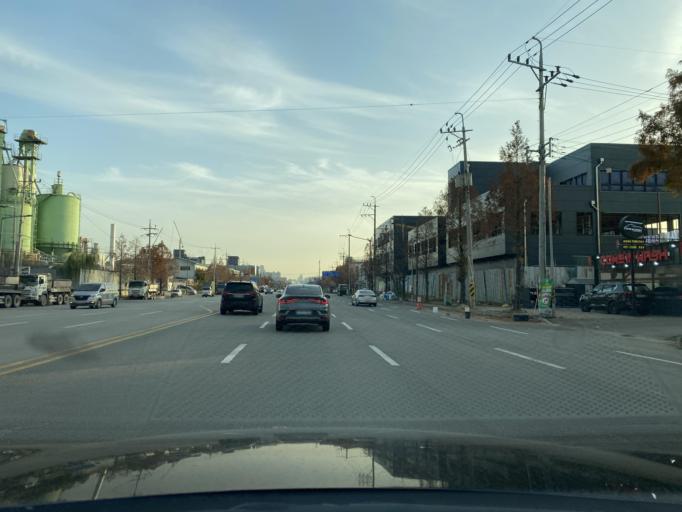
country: KR
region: Incheon
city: Incheon
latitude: 37.5031
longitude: 126.6616
